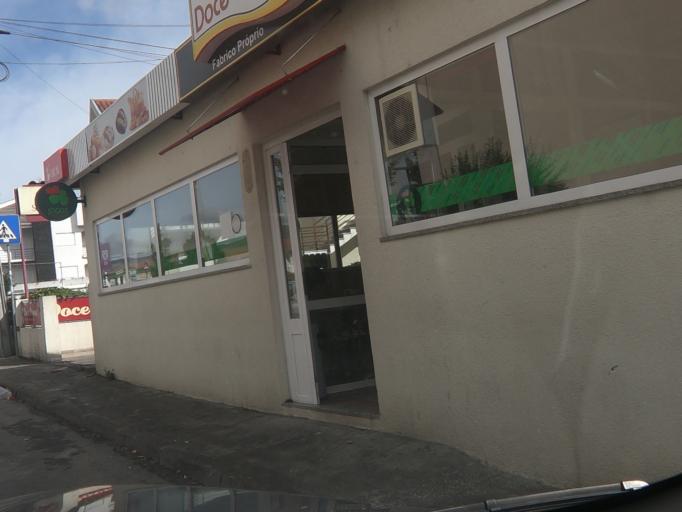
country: PT
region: Vila Real
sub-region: Vila Real
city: Vila Real
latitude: 41.2939
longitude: -7.7294
